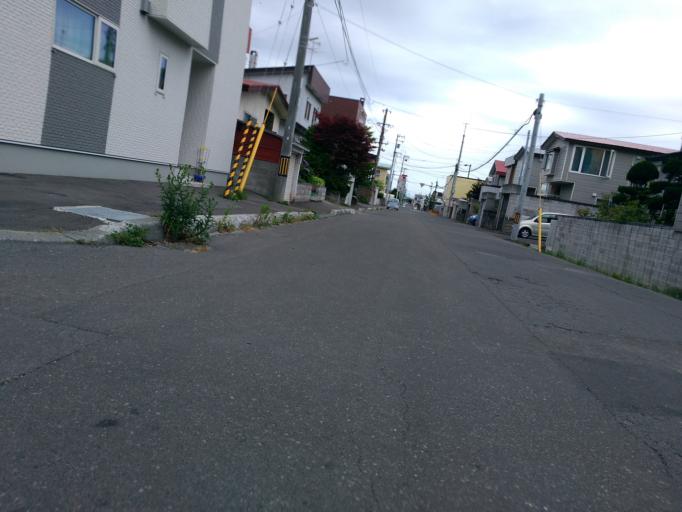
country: JP
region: Hokkaido
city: Ebetsu
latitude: 43.0829
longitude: 141.5238
